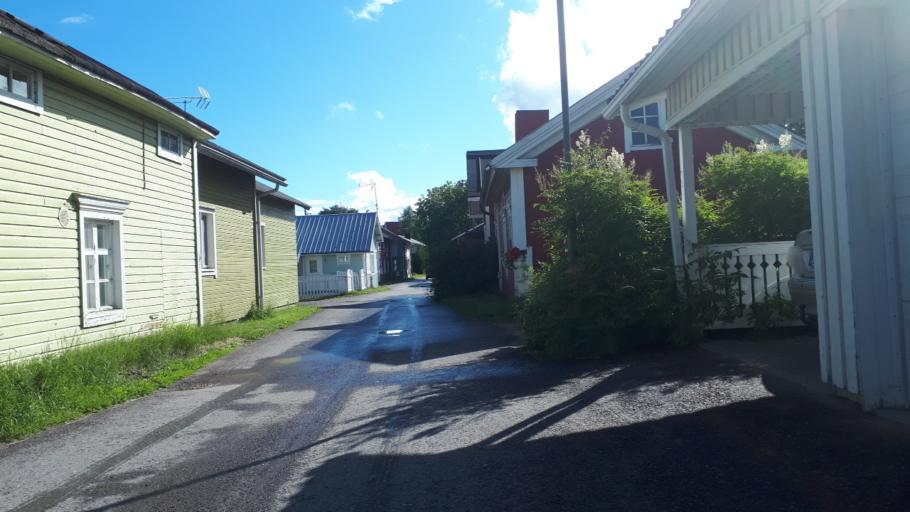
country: FI
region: Northern Ostrobothnia
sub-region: Oulunkaari
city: Ii
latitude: 65.3253
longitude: 25.3710
